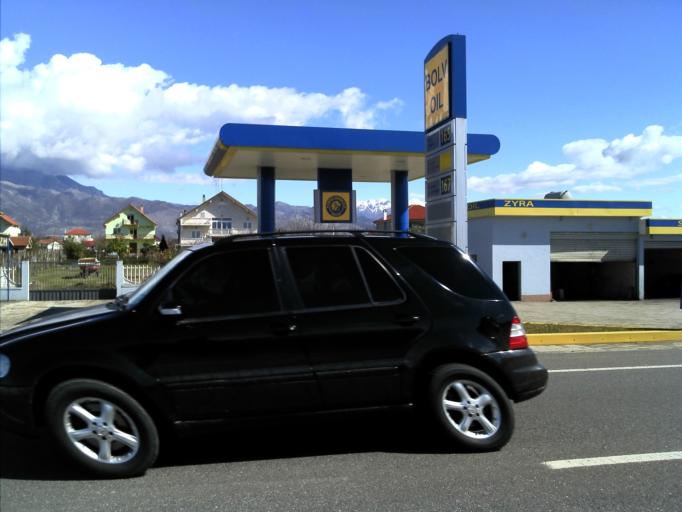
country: AL
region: Shkoder
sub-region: Rrethi i Malesia e Madhe
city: Grude-Fushe
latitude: 42.1299
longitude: 19.4909
